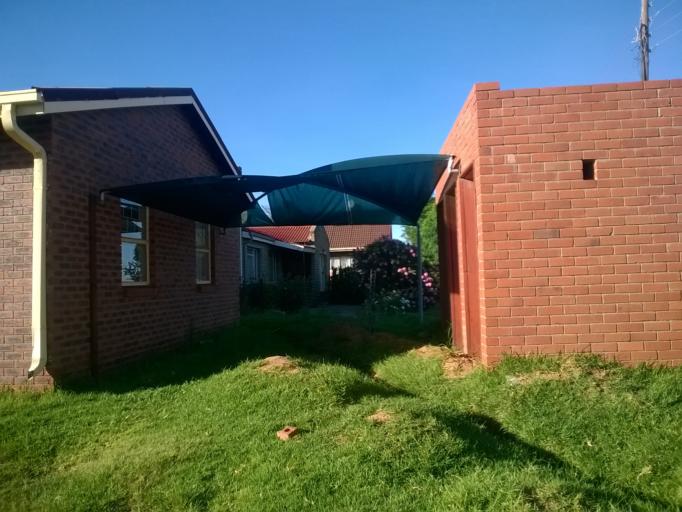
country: LS
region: Maseru
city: Maseru
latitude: -29.2891
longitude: 27.5280
